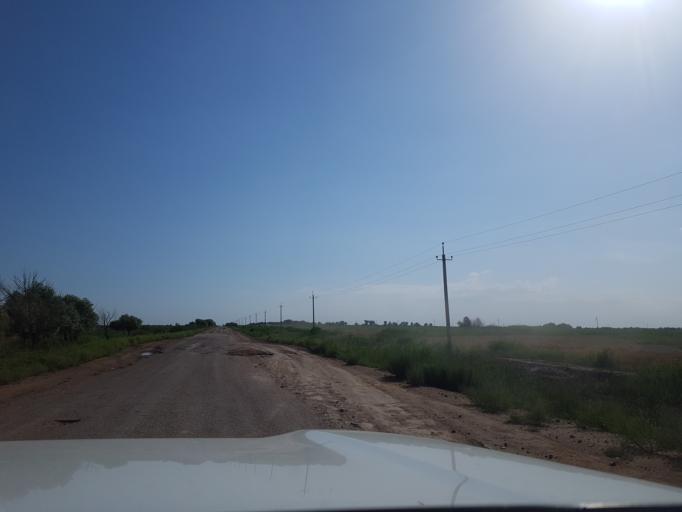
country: TM
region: Dasoguz
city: Koeneuergench
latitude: 42.0394
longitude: 58.8145
